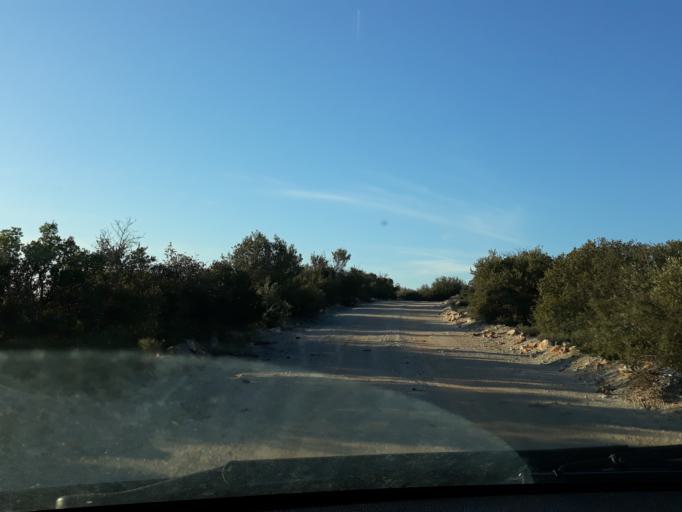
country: GR
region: Central Greece
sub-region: Nomos Voiotias
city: Asopia
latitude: 38.2670
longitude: 23.5313
